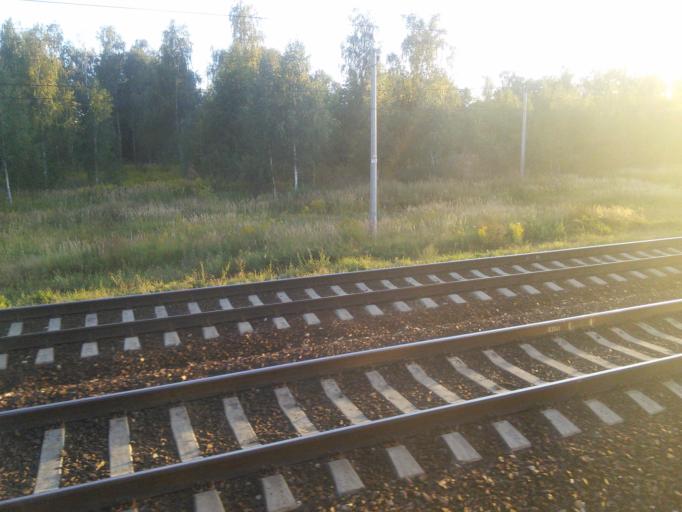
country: RU
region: Moskovskaya
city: Kupavna
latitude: 55.7488
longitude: 38.1375
